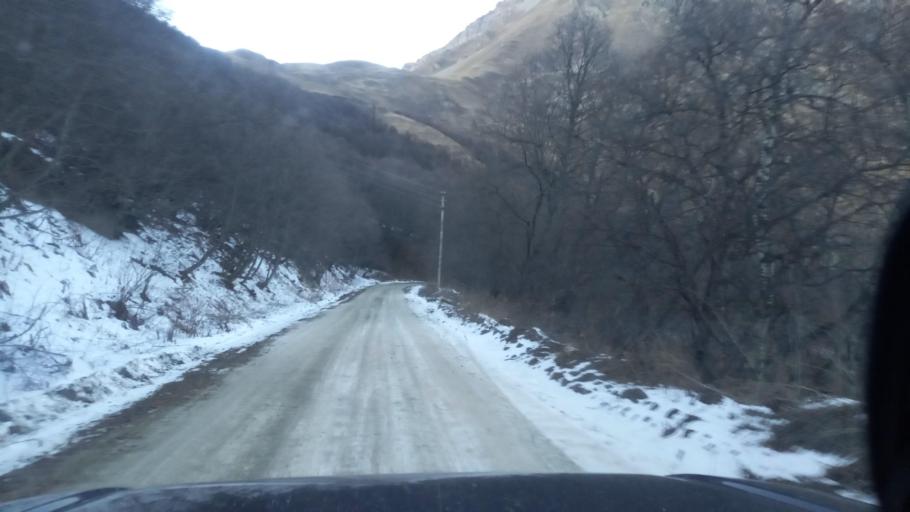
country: RU
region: Ingushetiya
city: Dzhayrakh
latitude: 42.8289
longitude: 44.5740
